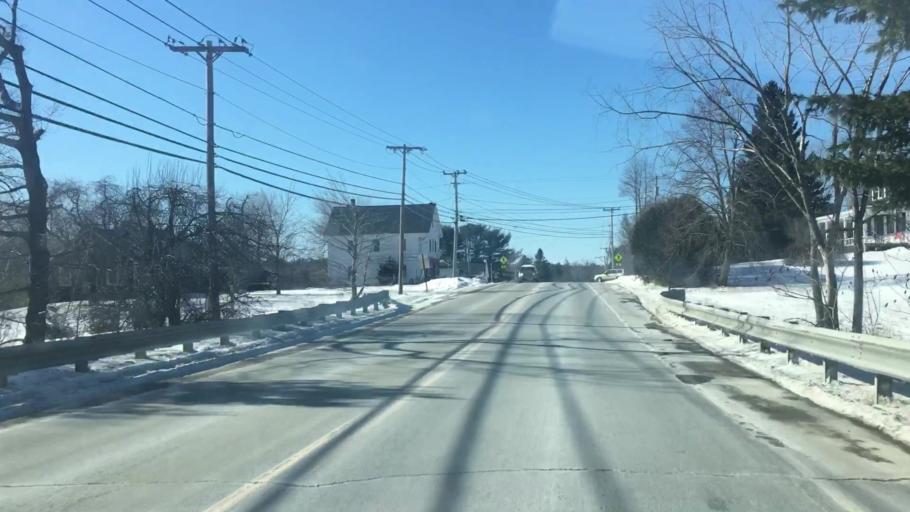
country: US
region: Maine
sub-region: Hancock County
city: Surry
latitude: 44.4955
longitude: -68.5009
